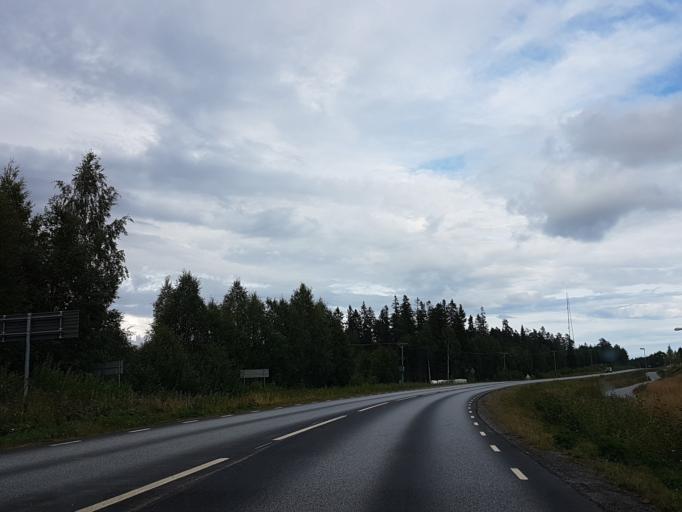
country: SE
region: Vaesterbotten
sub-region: Umea Kommun
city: Ersmark
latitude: 63.8083
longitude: 20.3693
